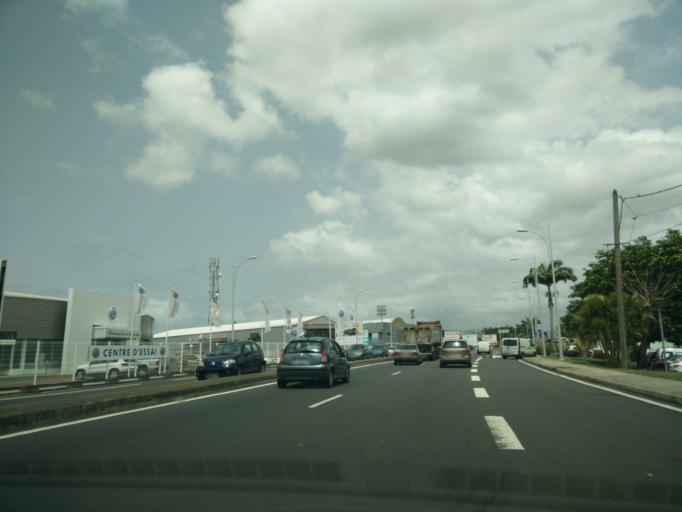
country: GP
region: Guadeloupe
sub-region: Guadeloupe
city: Baie-Mahault
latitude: 16.2403
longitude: -61.5857
